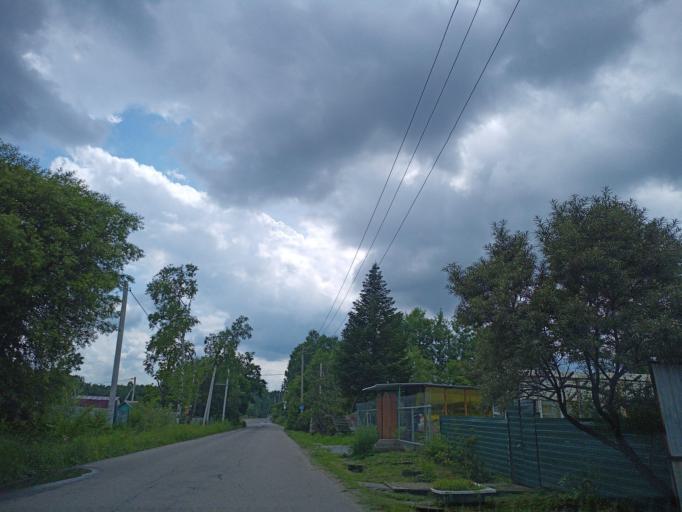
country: RU
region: Khabarovsk Krai
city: Korfovskiy
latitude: 48.3017
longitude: 135.0943
